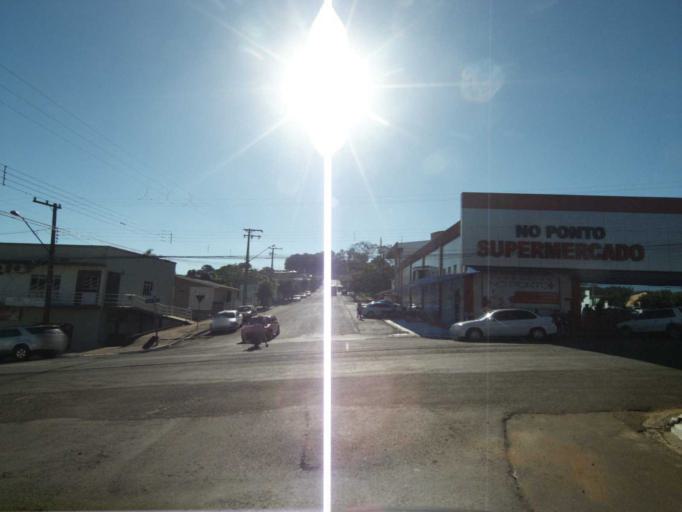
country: BR
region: Parana
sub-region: Coronel Vivida
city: Coronel Vivida
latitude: -25.9595
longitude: -52.8154
